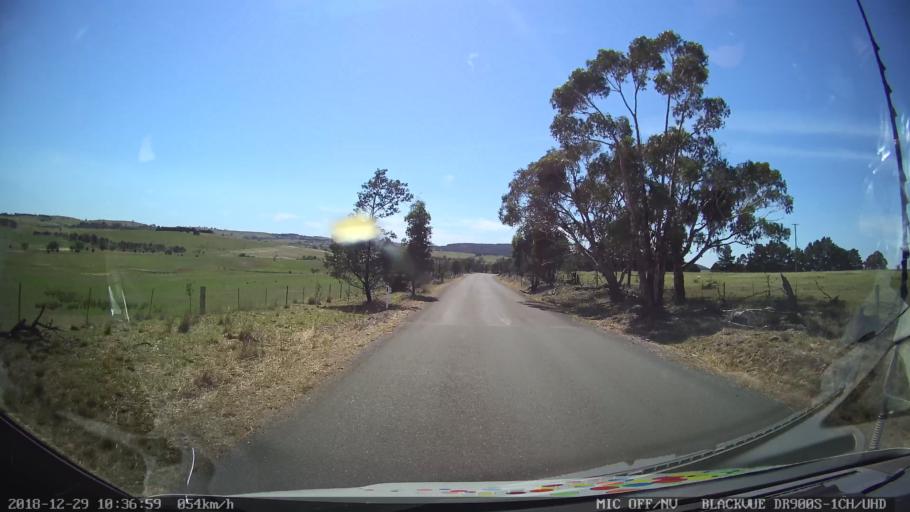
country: AU
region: New South Wales
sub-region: Yass Valley
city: Gundaroo
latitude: -34.9962
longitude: 149.4947
